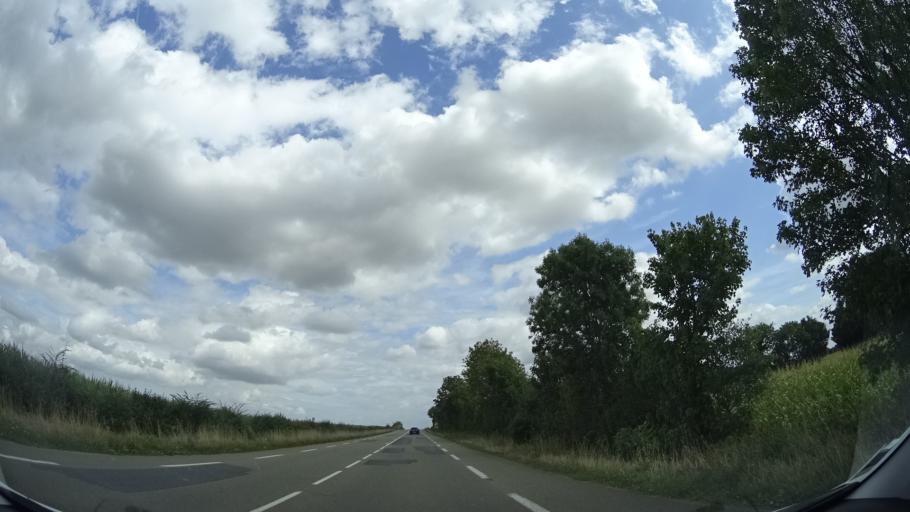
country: FR
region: Pays de la Loire
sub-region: Departement de la Mayenne
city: Bonchamp-les-Laval
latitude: 48.0688
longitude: -0.6792
